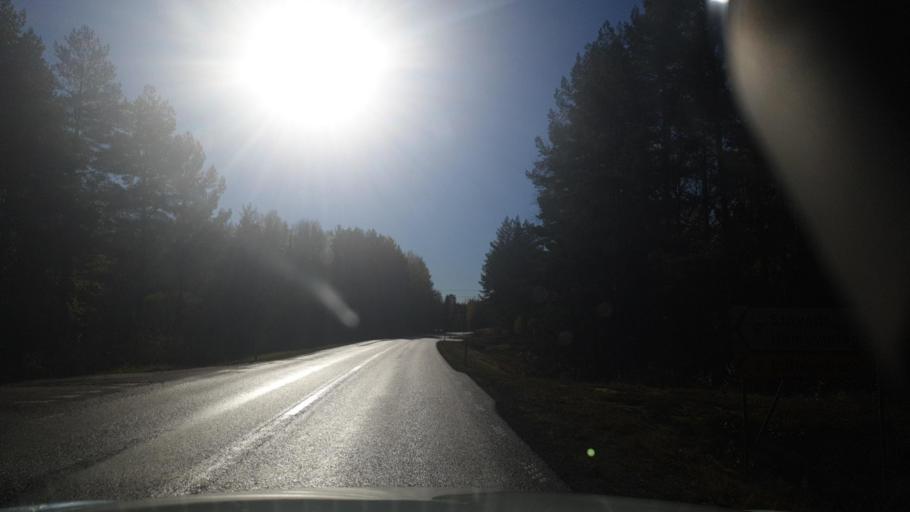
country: SE
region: Vaermland
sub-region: Arvika Kommun
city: Arvika
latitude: 59.5188
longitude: 12.7767
